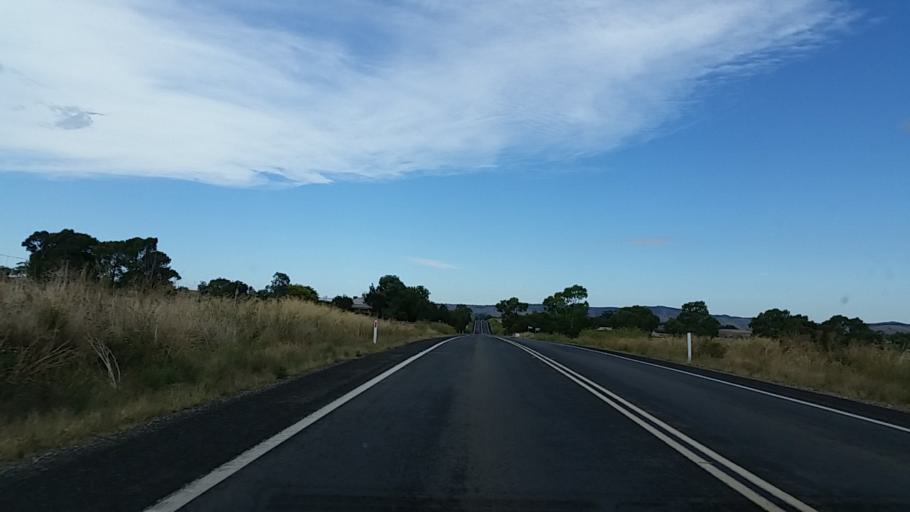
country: AU
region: South Australia
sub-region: Barossa
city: Tanunda
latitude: -34.5295
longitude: 138.8956
